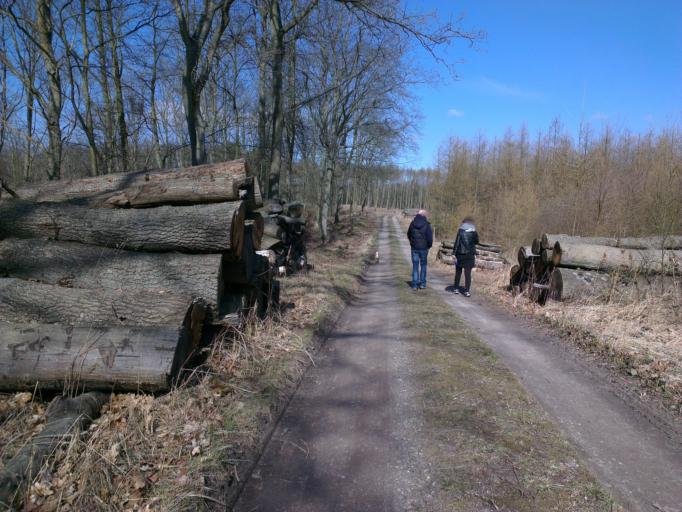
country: DK
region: Capital Region
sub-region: Frederikssund Kommune
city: Jaegerspris
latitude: 55.9096
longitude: 11.9413
